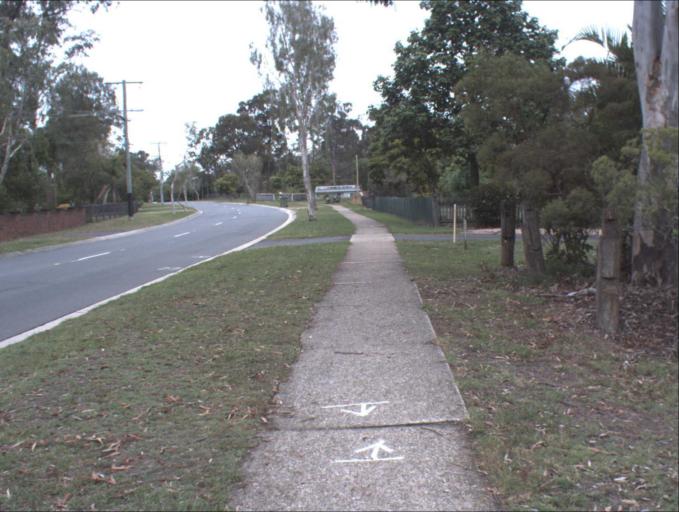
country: AU
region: Queensland
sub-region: Brisbane
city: Forest Lake
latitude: -27.6597
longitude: 153.0073
